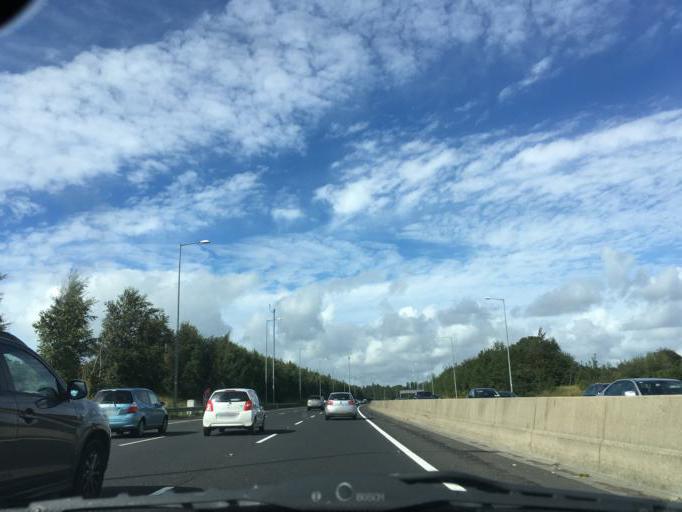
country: IE
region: Leinster
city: Ballyboden
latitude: 53.2673
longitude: -6.2893
